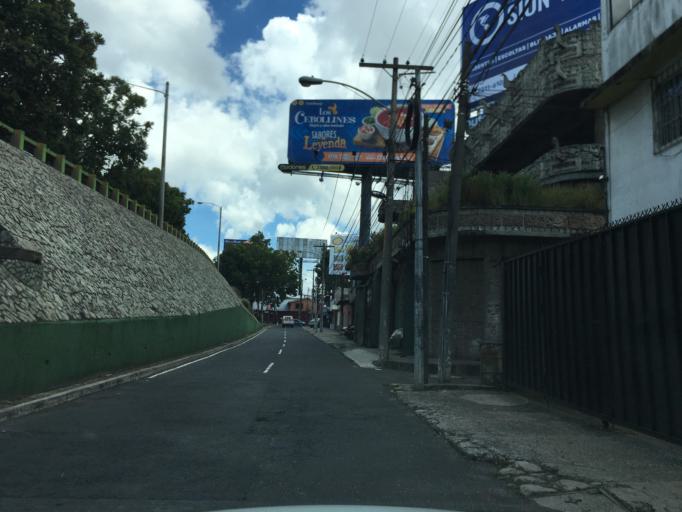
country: GT
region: Guatemala
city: Guatemala City
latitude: 14.6114
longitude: -90.5550
